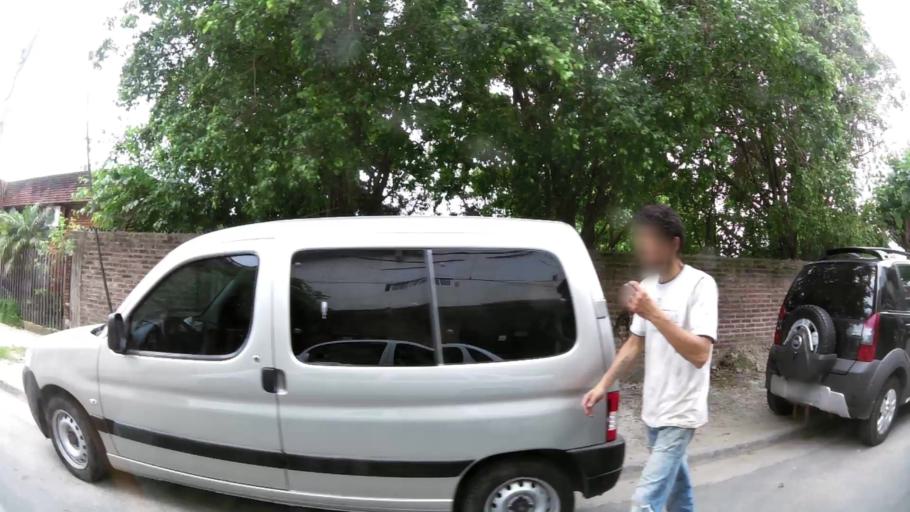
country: AR
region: Buenos Aires
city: San Justo
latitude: -34.6663
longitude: -58.5437
